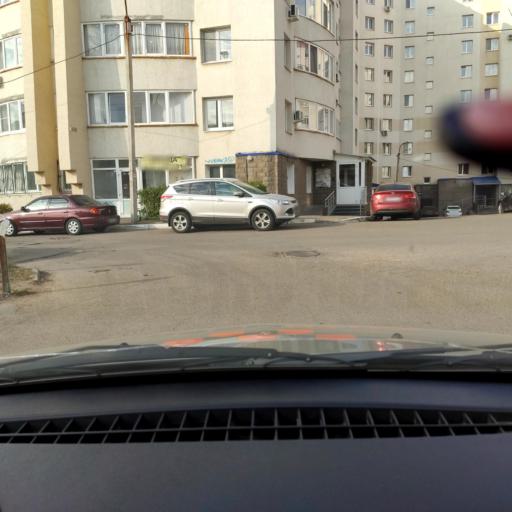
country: RU
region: Bashkortostan
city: Ufa
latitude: 54.7457
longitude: 55.9555
